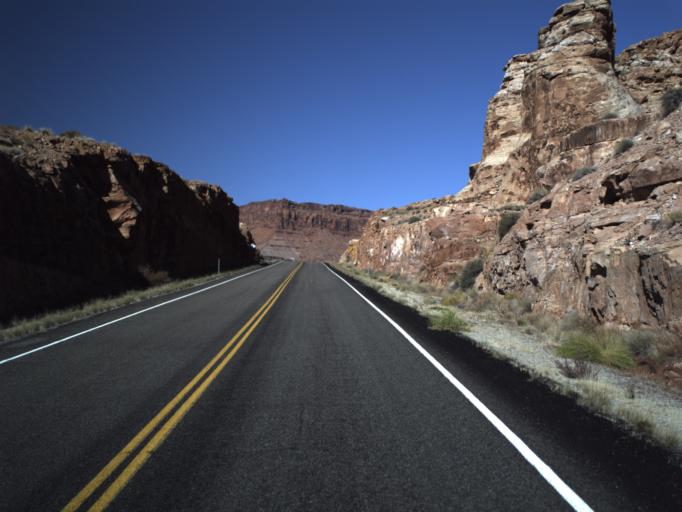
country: US
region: Utah
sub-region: San Juan County
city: Blanding
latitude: 37.8940
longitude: -110.3734
